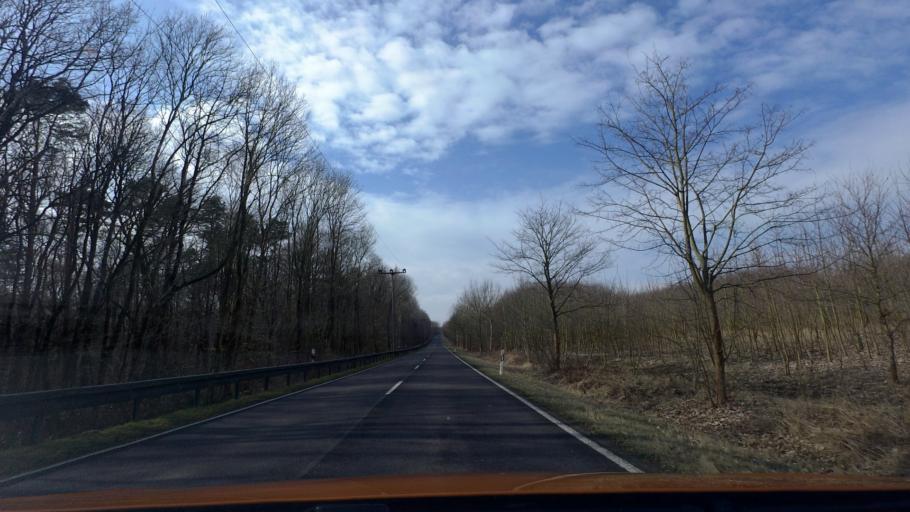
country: DE
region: Saxony-Anhalt
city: Beendorf
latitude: 52.2198
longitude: 11.0906
